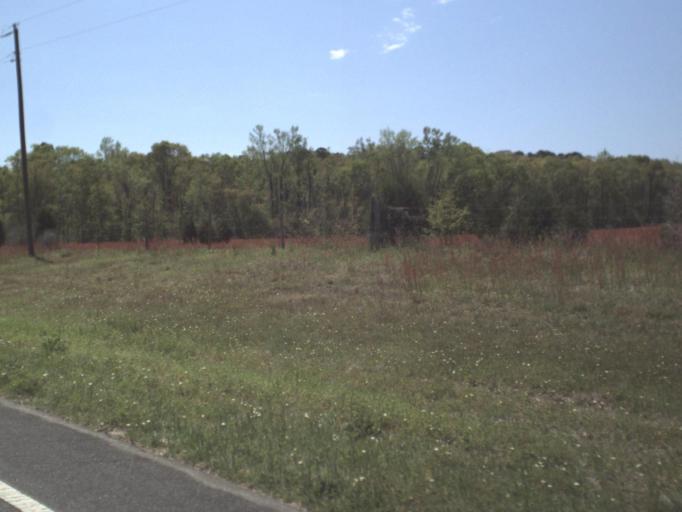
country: US
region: Alabama
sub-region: Geneva County
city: Geneva
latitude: 30.8451
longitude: -85.9492
